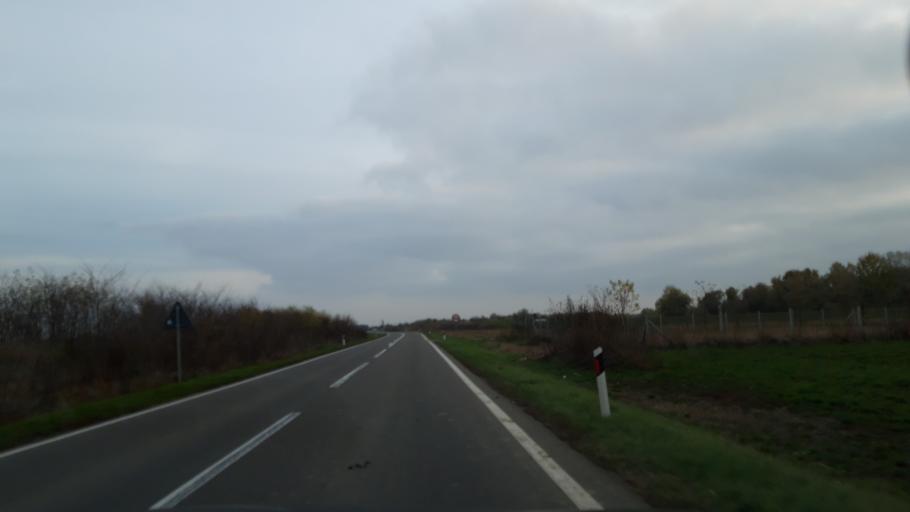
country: RS
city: Sanad
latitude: 45.9910
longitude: 20.1081
